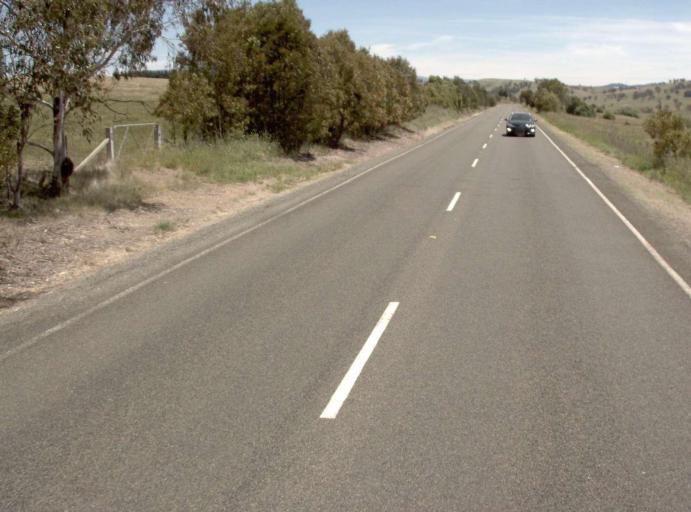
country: AU
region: Victoria
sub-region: Alpine
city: Mount Beauty
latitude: -37.1444
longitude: 147.6474
